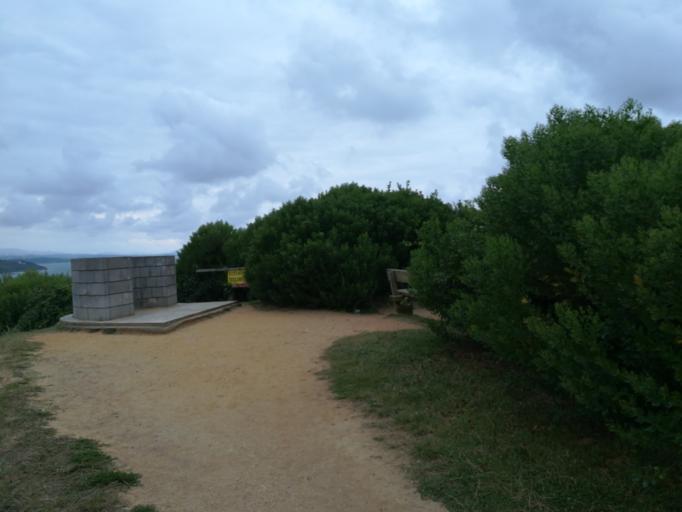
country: FR
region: Aquitaine
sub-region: Departement des Pyrenees-Atlantiques
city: Bidart
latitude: 43.4391
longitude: -1.5932
